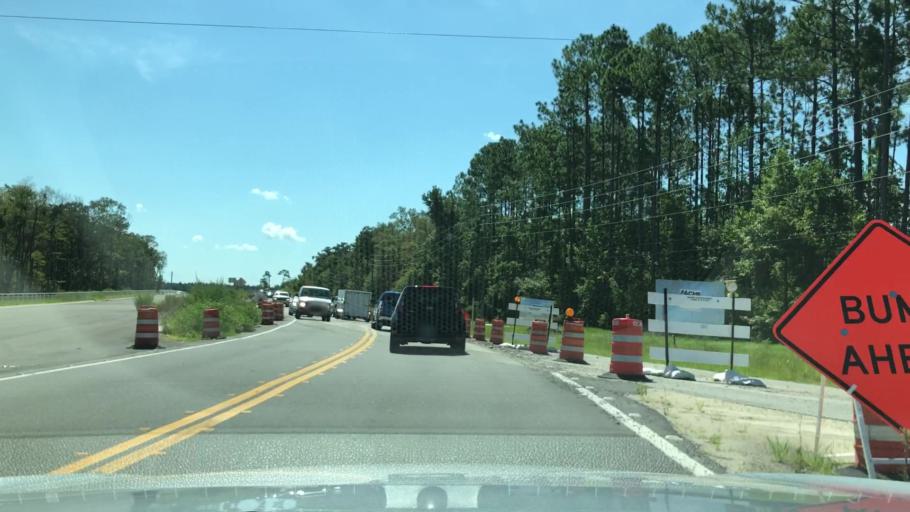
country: US
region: Florida
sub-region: Saint Johns County
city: Fruit Cove
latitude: 30.1003
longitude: -81.5292
